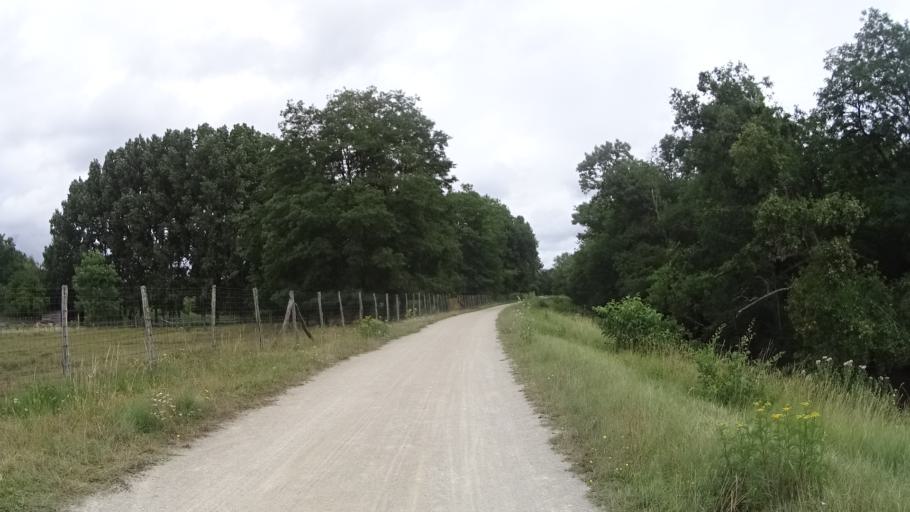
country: FR
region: Centre
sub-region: Departement du Loiret
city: Baule
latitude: 47.8136
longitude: 1.6851
